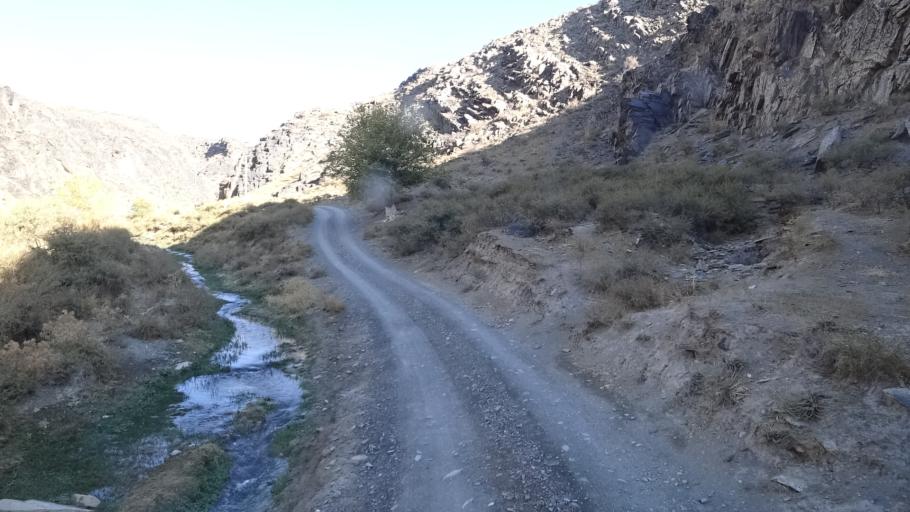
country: UZ
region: Navoiy
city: Nurota
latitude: 40.3045
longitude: 65.6169
